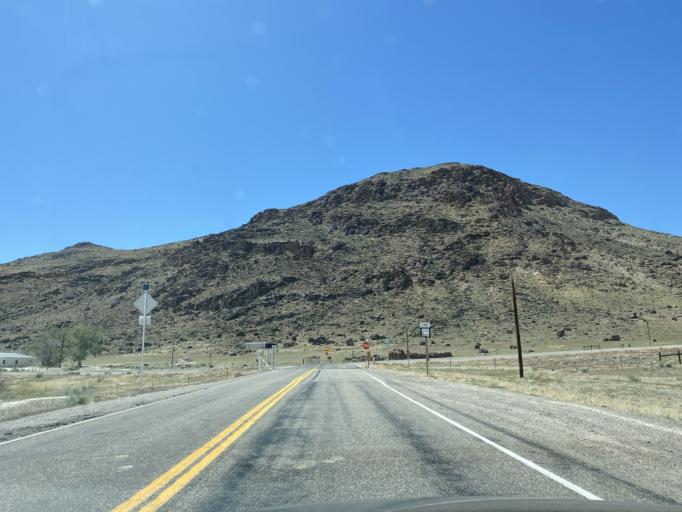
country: US
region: Nevada
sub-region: Nye County
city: Tonopah
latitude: 38.1909
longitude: -116.3686
